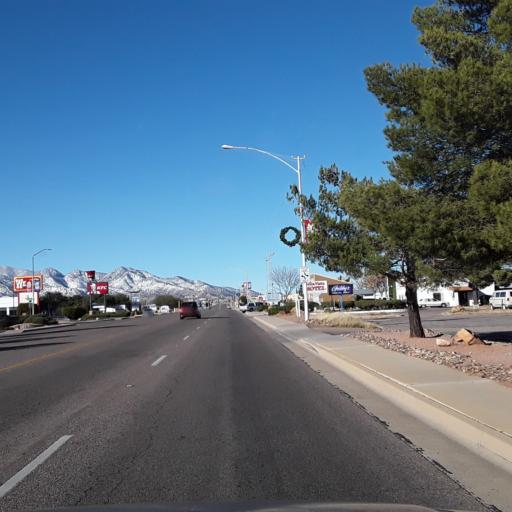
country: US
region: Arizona
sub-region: Cochise County
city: Sierra Vista
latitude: 31.5547
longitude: -110.2859
